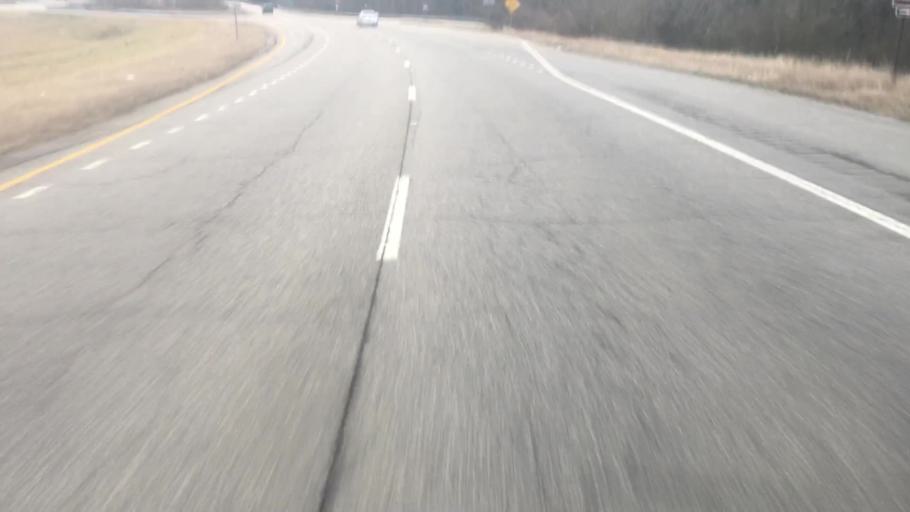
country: US
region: Alabama
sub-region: Walker County
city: Cordova
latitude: 33.8075
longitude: -87.1447
